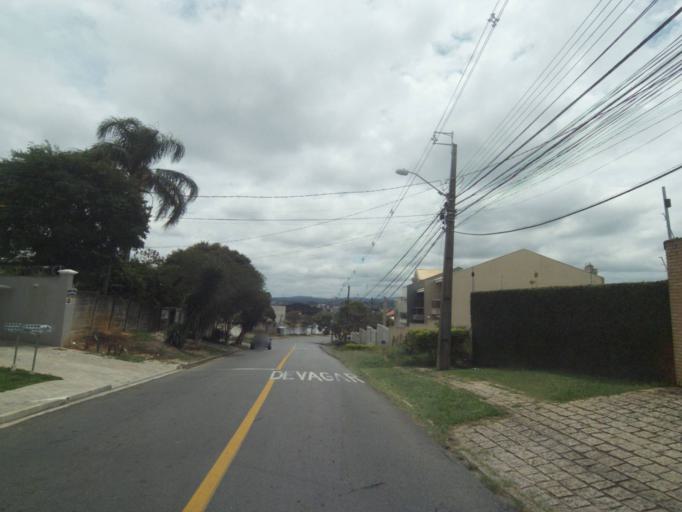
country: BR
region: Parana
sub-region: Curitiba
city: Curitiba
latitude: -25.3927
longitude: -49.2871
